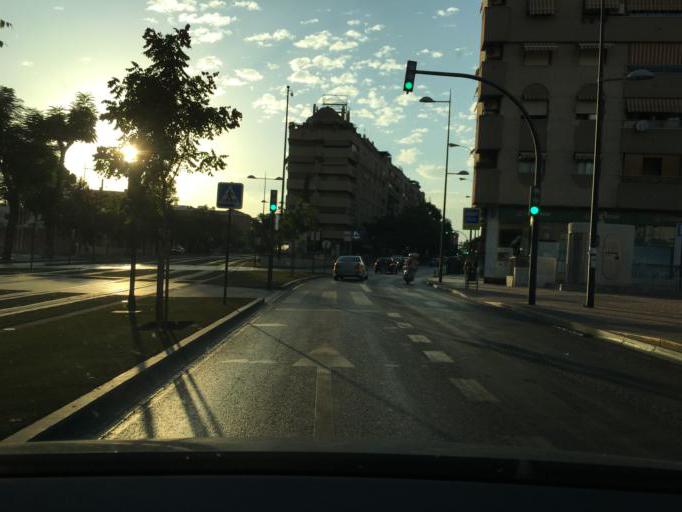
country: ES
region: Andalusia
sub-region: Provincia de Granada
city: Granada
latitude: 37.1872
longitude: -3.6106
